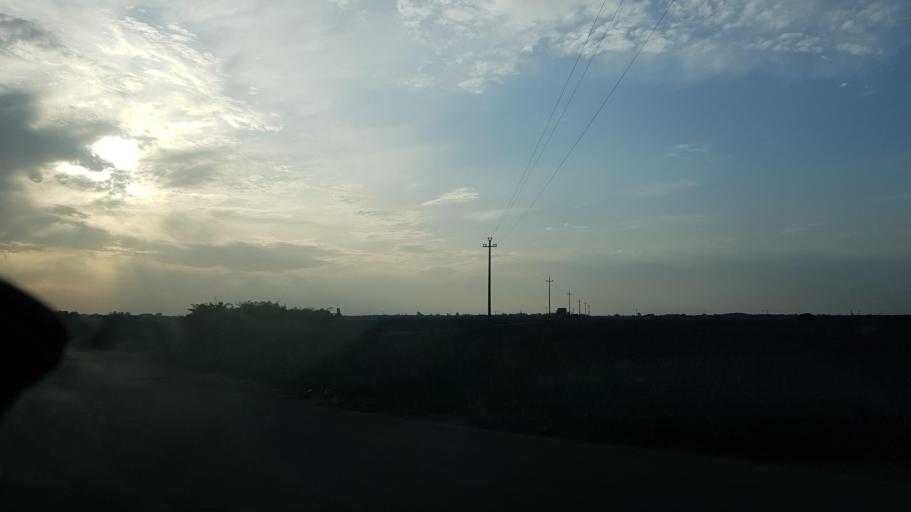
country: IT
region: Apulia
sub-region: Provincia di Brindisi
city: Mesagne
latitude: 40.5259
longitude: 17.8338
